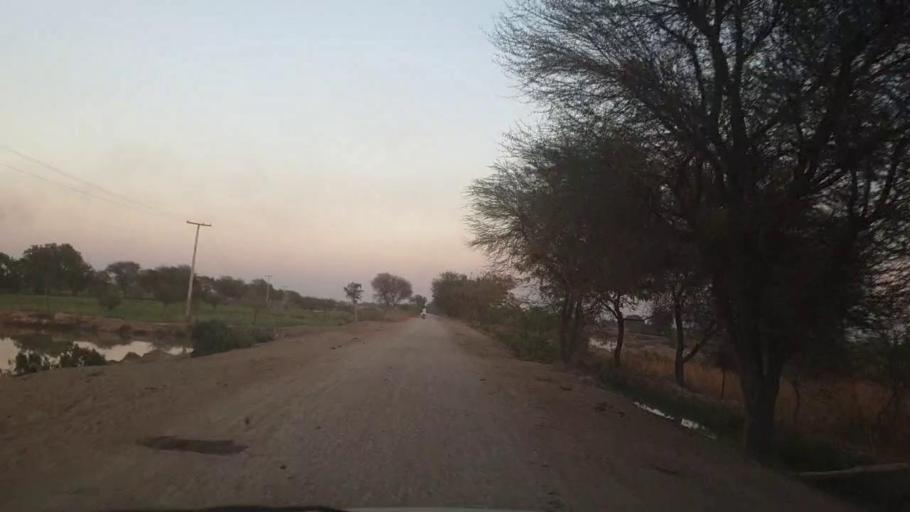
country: PK
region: Sindh
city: Mirpur Khas
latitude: 25.4970
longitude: 69.0406
